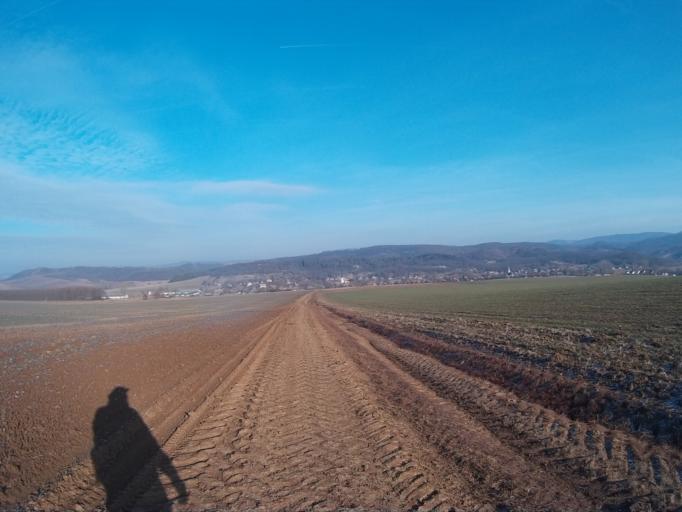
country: HU
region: Nograd
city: Bercel
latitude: 47.9413
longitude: 19.4307
